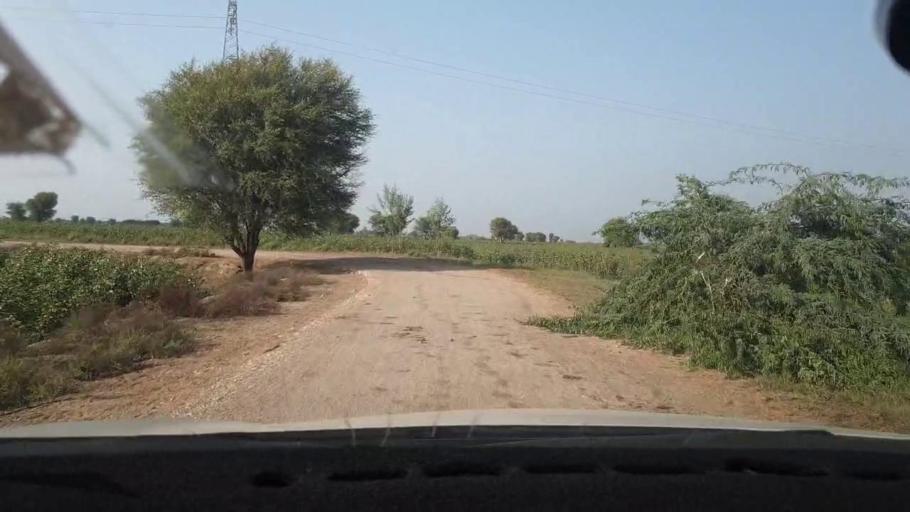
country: PK
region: Sindh
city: Berani
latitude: 25.7514
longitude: 68.7756
